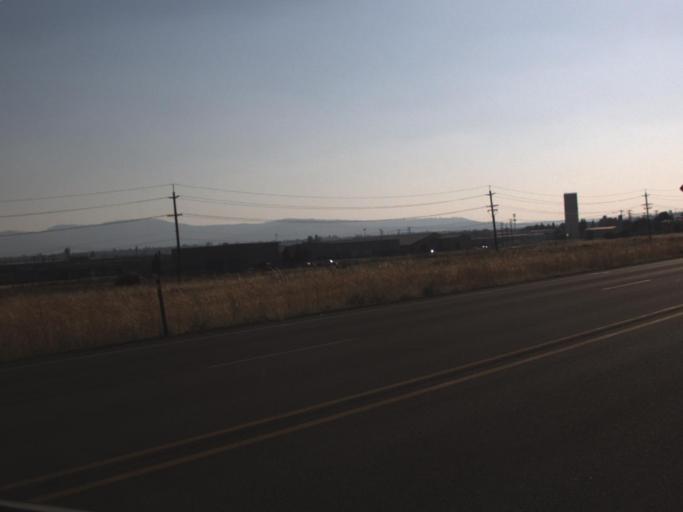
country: US
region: Washington
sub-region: Spokane County
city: Trentwood
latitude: 47.6964
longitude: -117.1818
